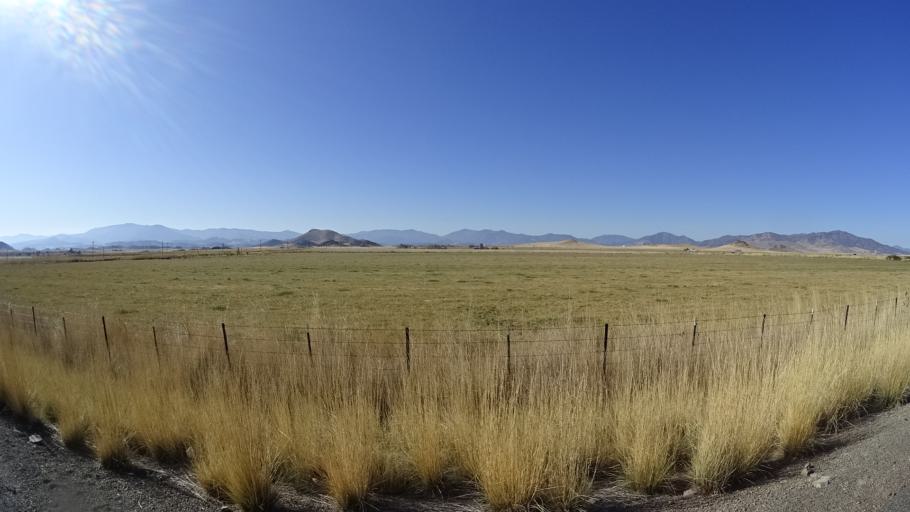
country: US
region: California
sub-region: Siskiyou County
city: Montague
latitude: 41.7283
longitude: -122.4574
